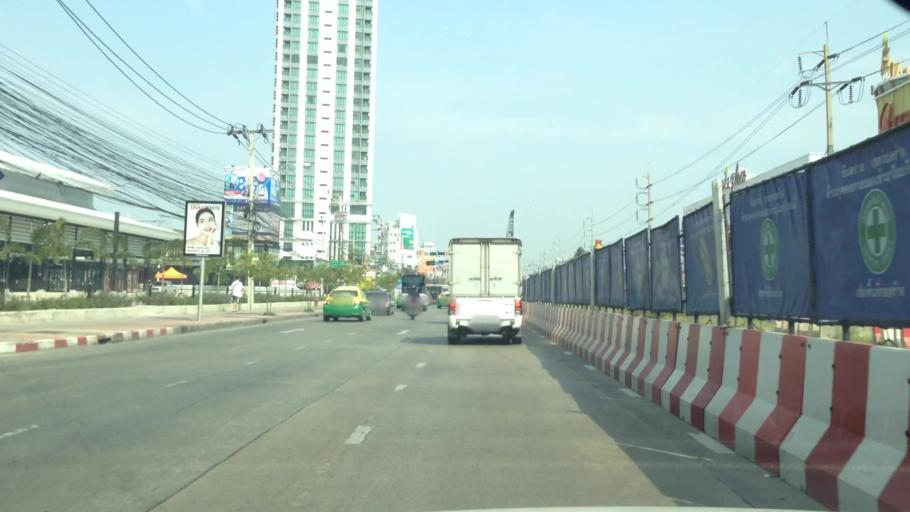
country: TH
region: Bangkok
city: Bang Na
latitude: 13.6882
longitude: 100.6468
